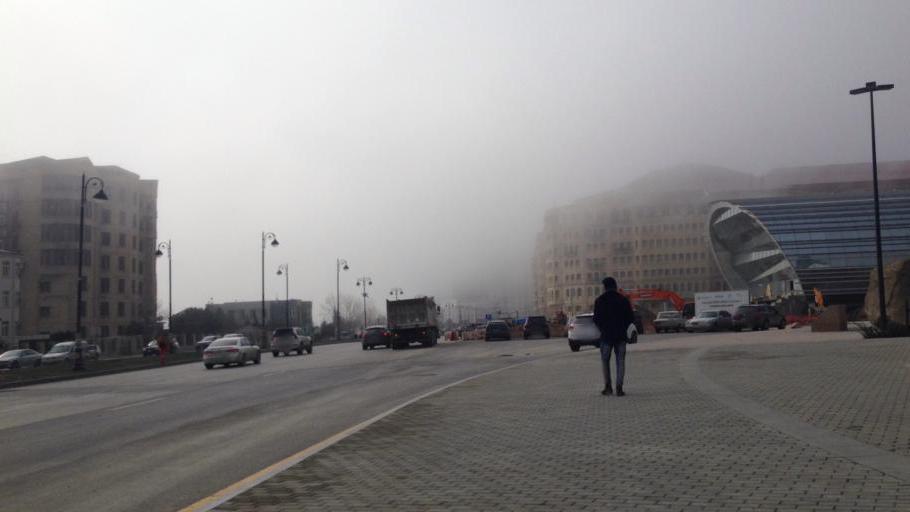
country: AZ
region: Baki
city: Baku
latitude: 40.3795
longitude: 49.8822
